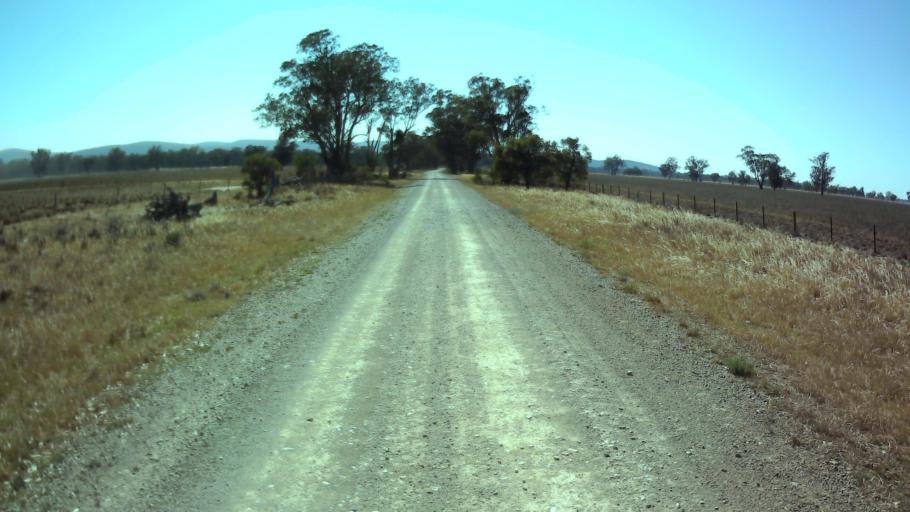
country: AU
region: New South Wales
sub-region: Weddin
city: Grenfell
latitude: -33.9442
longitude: 147.8620
